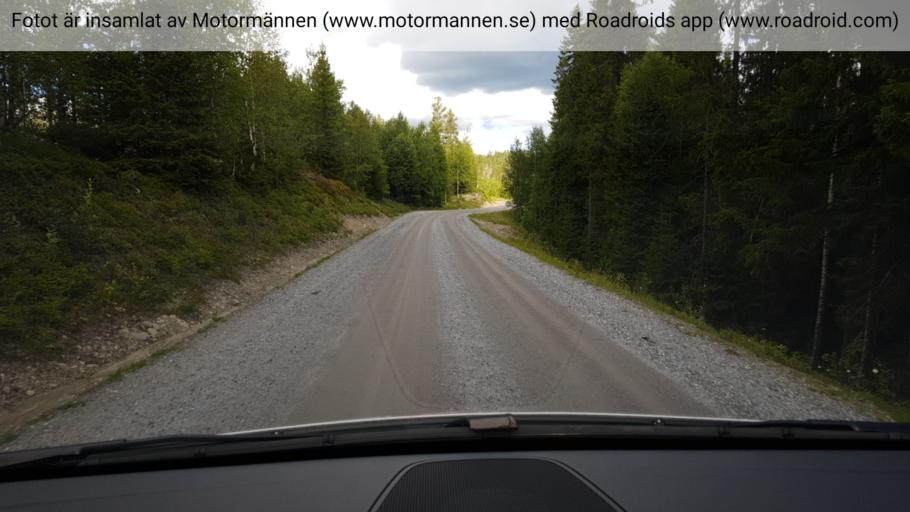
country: SE
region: Jaemtland
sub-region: Braecke Kommun
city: Braecke
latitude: 62.9942
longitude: 15.7257
